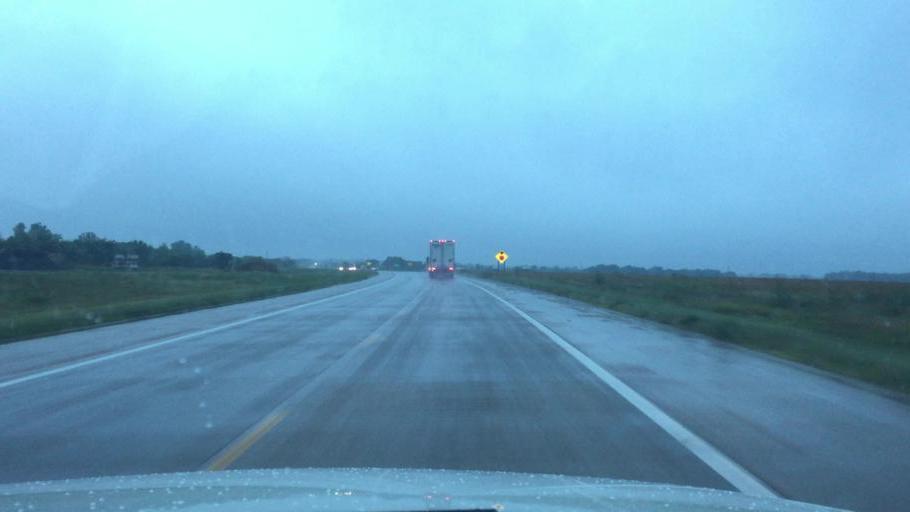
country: US
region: Kansas
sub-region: Neosho County
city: Chanute
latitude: 37.5335
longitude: -95.4714
